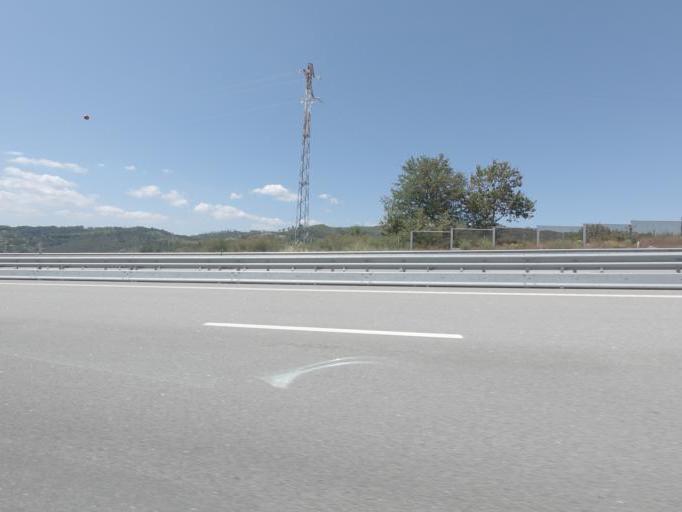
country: PT
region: Porto
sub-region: Amarante
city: Amarante
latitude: 41.2614
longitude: -8.0116
